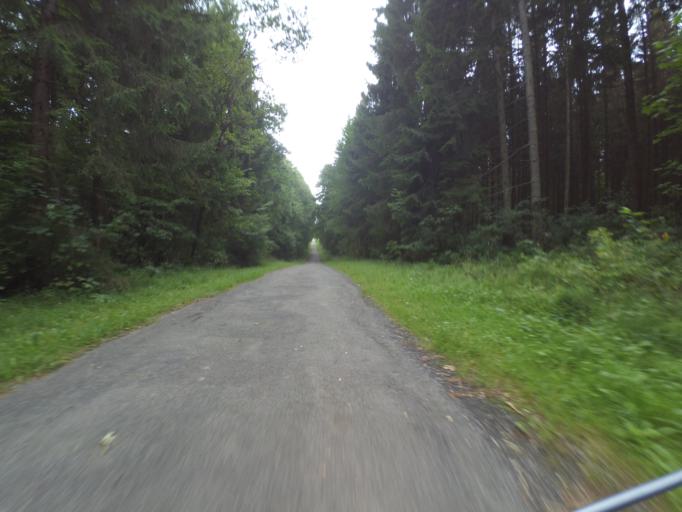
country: DE
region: Baden-Wuerttemberg
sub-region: Freiburg Region
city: Donaueschingen
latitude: 47.9584
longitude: 8.4672
